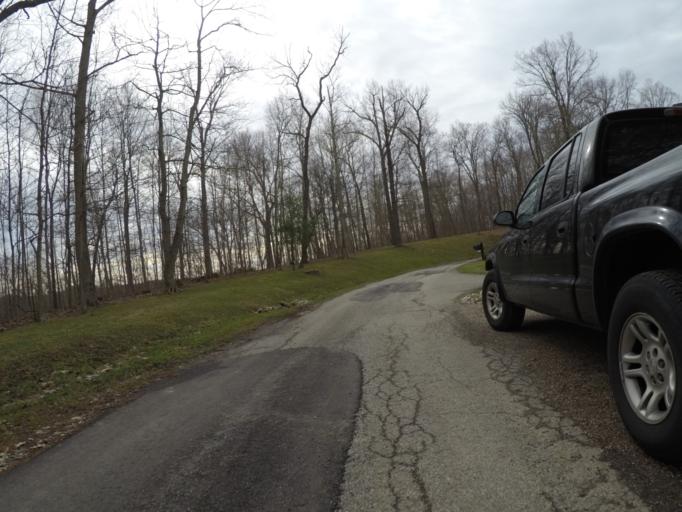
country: US
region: Ohio
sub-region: Lawrence County
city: Burlington
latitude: 38.3797
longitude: -82.5057
